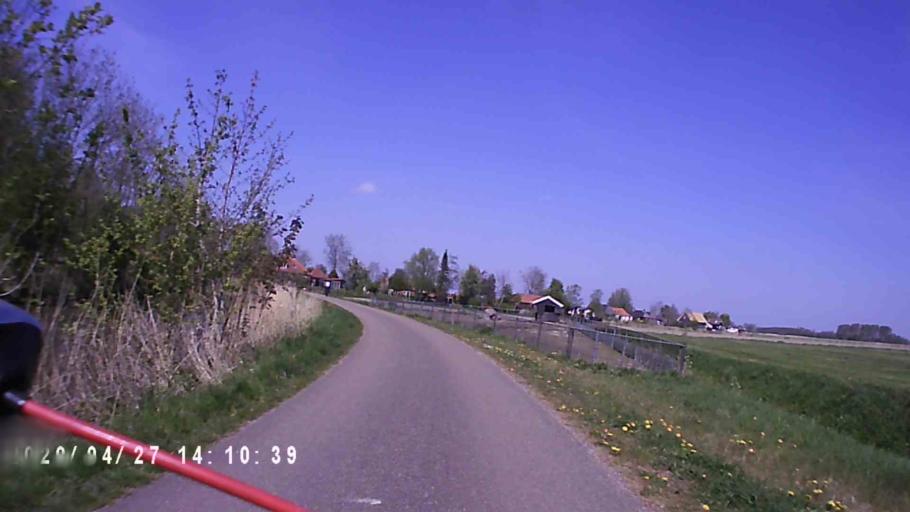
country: NL
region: Groningen
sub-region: Gemeente Zuidhorn
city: Oldehove
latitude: 53.3513
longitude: 6.3917
